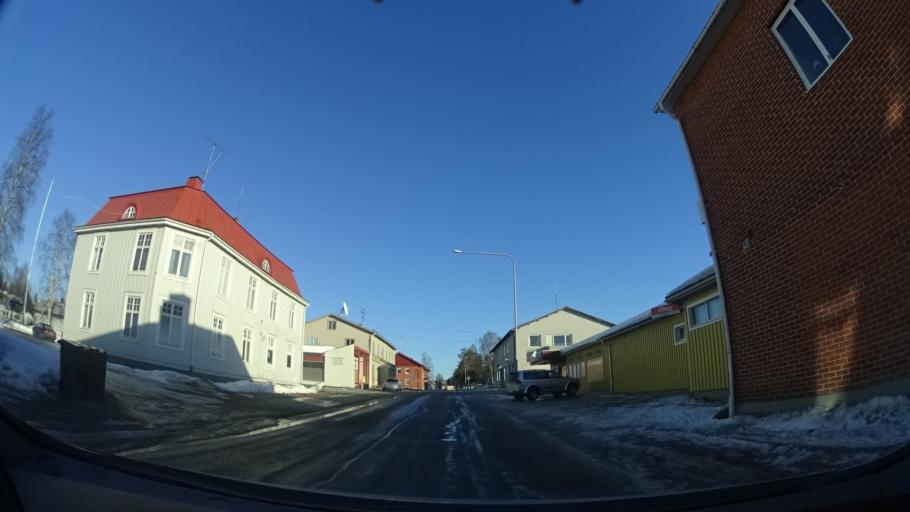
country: SE
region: Vaesterbotten
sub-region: Skelleftea Kommun
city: Langsele
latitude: 65.0597
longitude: 20.0370
